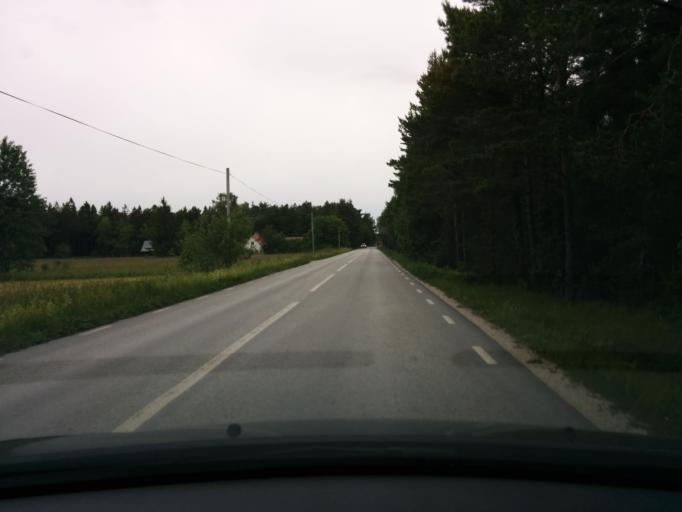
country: SE
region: Gotland
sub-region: Gotland
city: Slite
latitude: 57.6599
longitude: 18.7723
